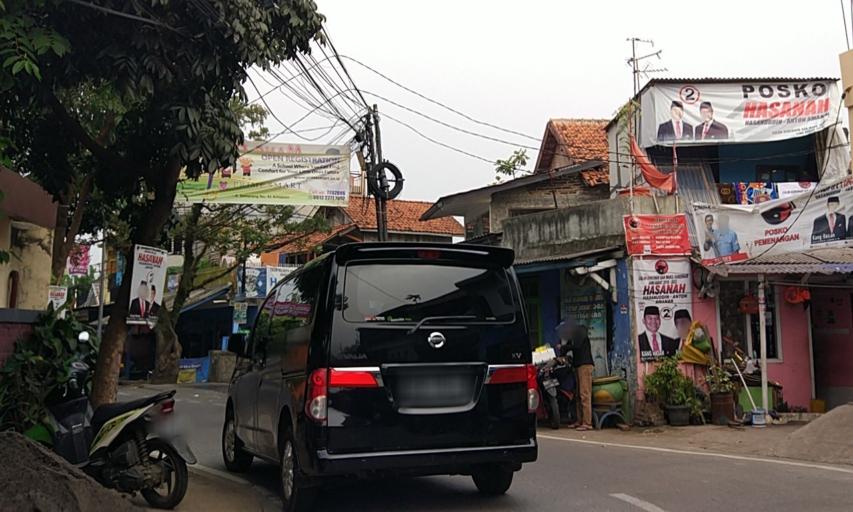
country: ID
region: West Java
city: Bandung
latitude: -6.9103
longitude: 107.6578
